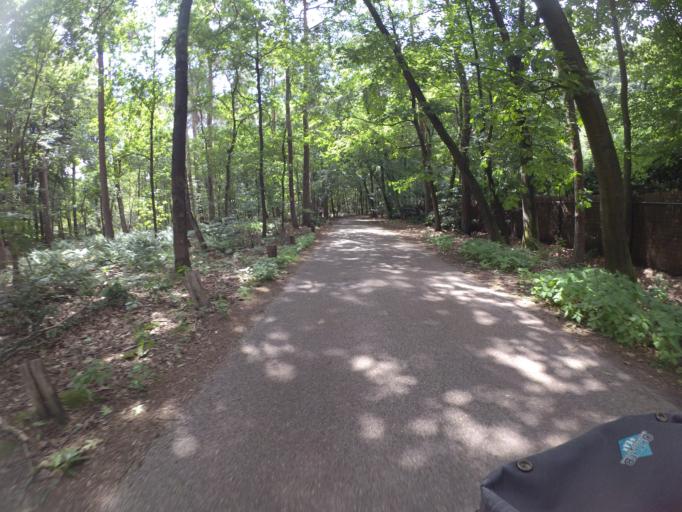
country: NL
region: North Brabant
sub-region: Gemeente Oisterwijk
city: Oisterwijk
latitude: 51.5640
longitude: 5.2023
